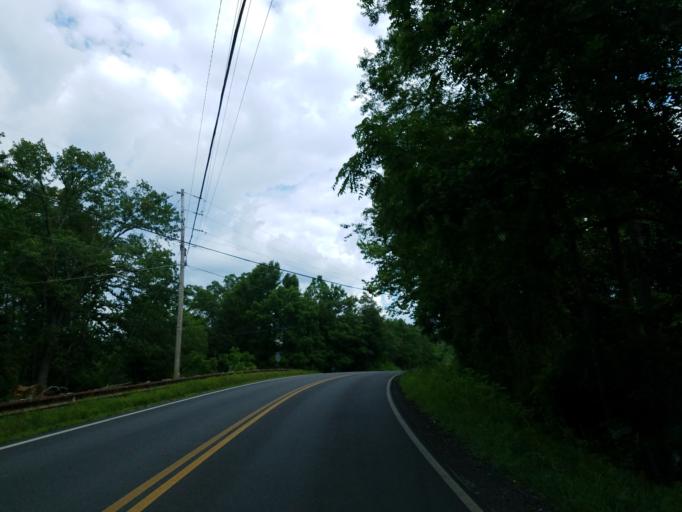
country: US
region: Georgia
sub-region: Fannin County
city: Blue Ridge
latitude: 34.8630
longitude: -84.3039
